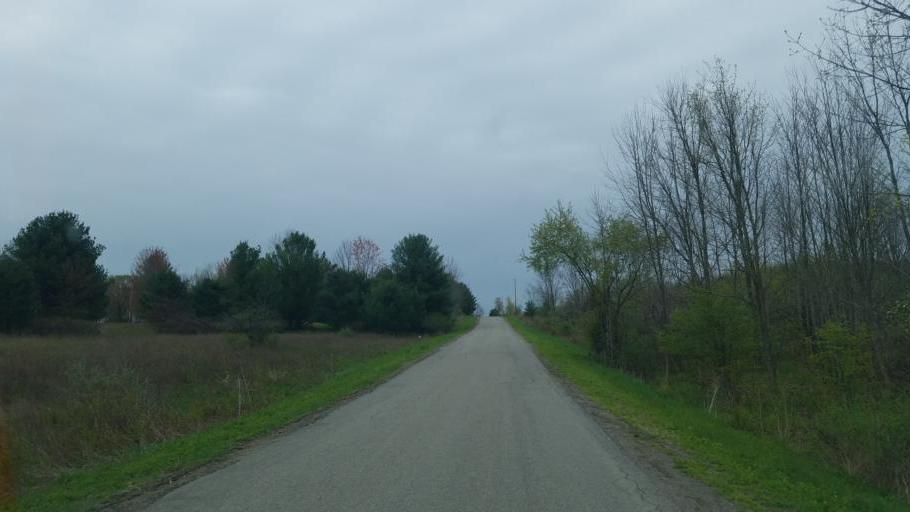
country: US
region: Pennsylvania
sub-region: Tioga County
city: Elkland
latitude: 42.0736
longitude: -77.4585
